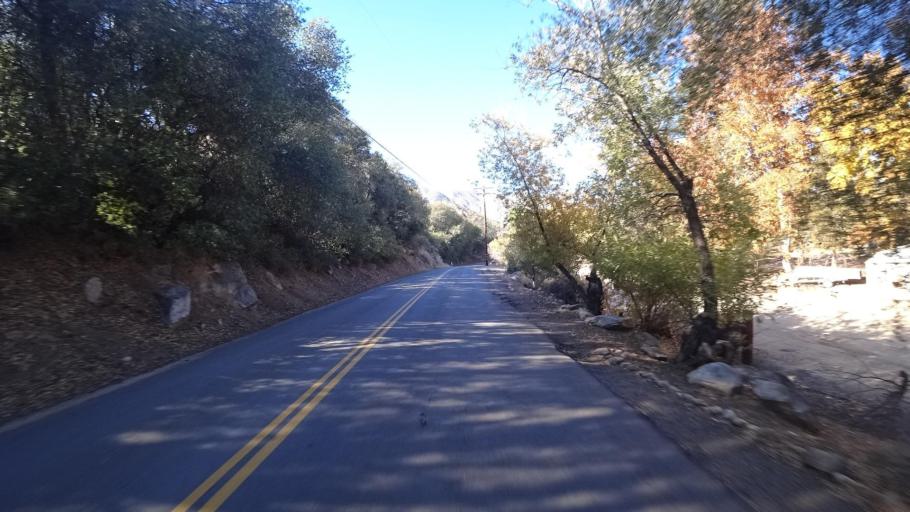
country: US
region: California
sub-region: Kern County
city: Kernville
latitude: 35.7728
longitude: -118.4411
